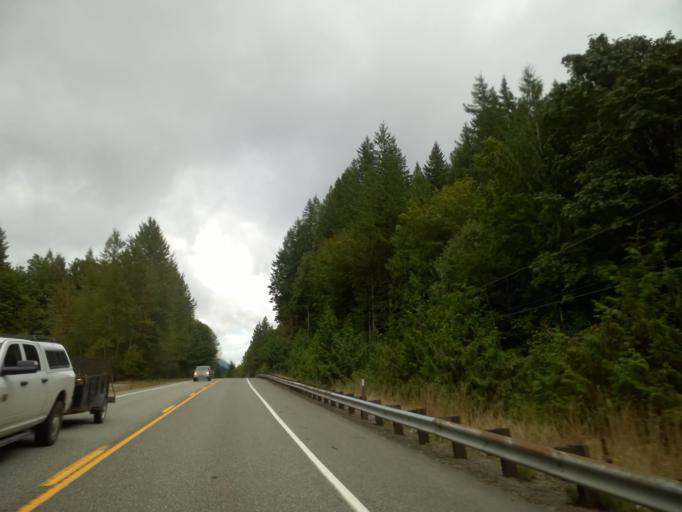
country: US
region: Washington
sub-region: Snohomish County
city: Gold Bar
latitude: 47.8056
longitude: -121.5298
